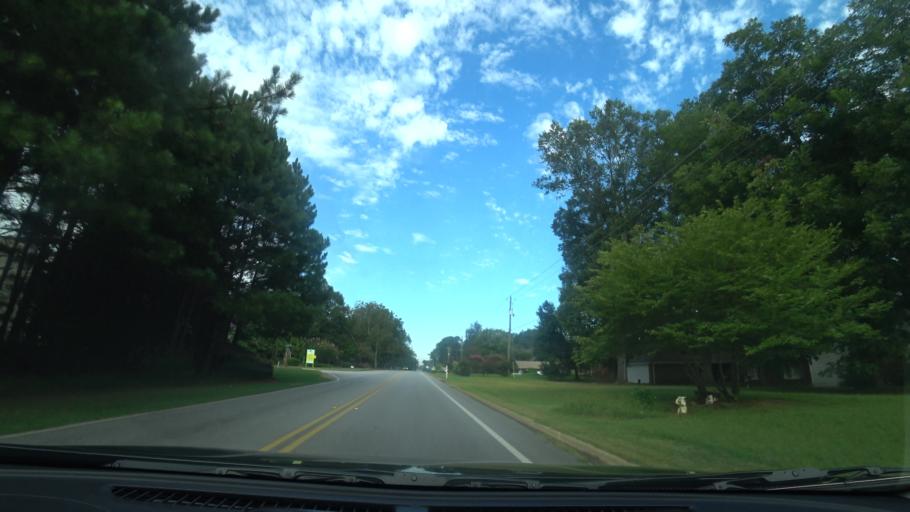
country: US
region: Georgia
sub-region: Newton County
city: Oakwood
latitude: 33.6123
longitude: -83.9602
